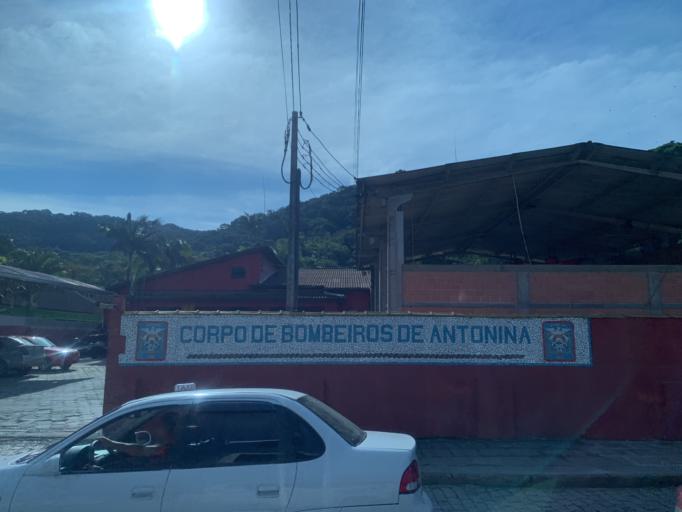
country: BR
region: Parana
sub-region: Antonina
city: Antonina
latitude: -25.4304
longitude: -48.7165
